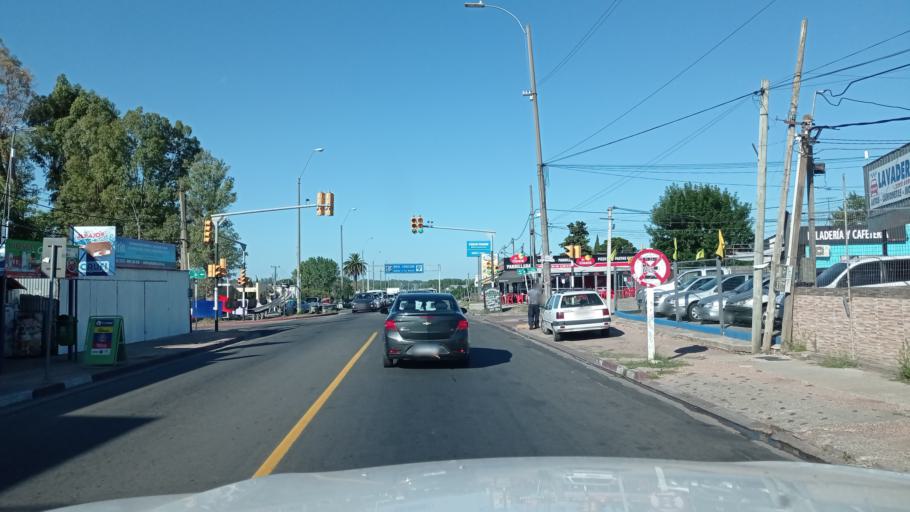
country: UY
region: Canelones
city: Pando
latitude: -34.7217
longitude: -55.9557
